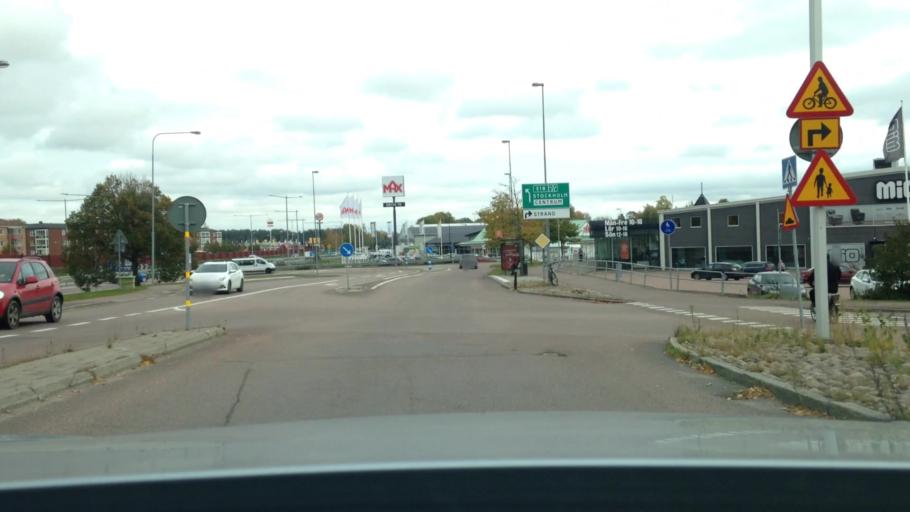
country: SE
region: Vaermland
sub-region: Karlstads Kommun
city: Karlstad
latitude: 59.3810
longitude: 13.4649
